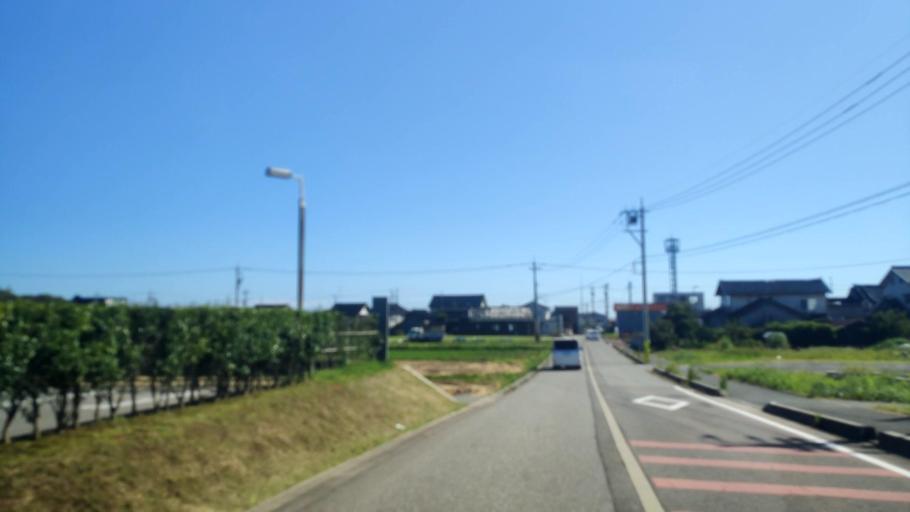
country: JP
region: Ishikawa
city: Nanao
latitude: 37.4427
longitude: 137.2705
